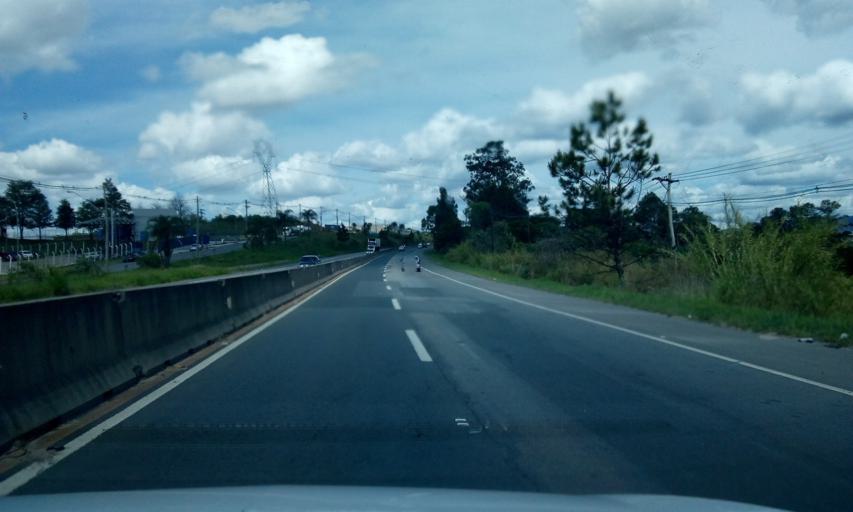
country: BR
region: Sao Paulo
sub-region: Itupeva
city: Itupeva
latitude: -23.1627
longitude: -47.0170
